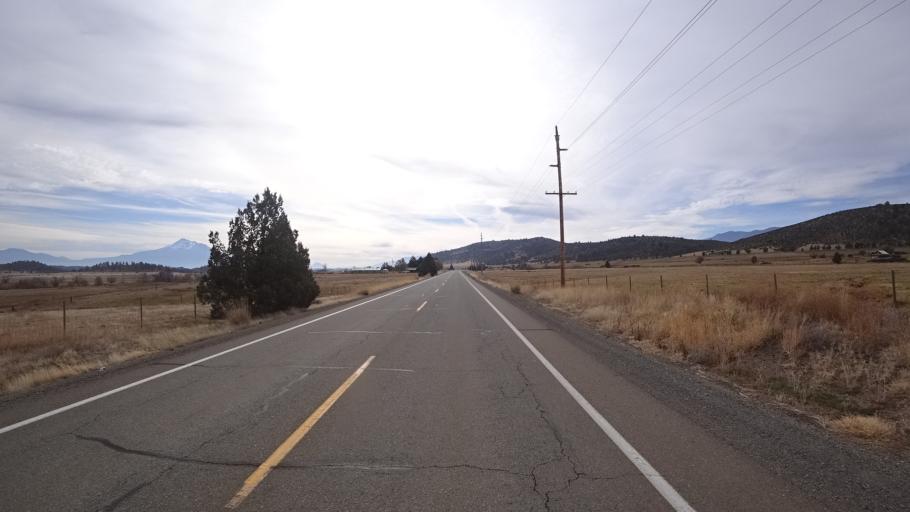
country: US
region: California
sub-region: Siskiyou County
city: Montague
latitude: 41.6938
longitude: -122.5350
